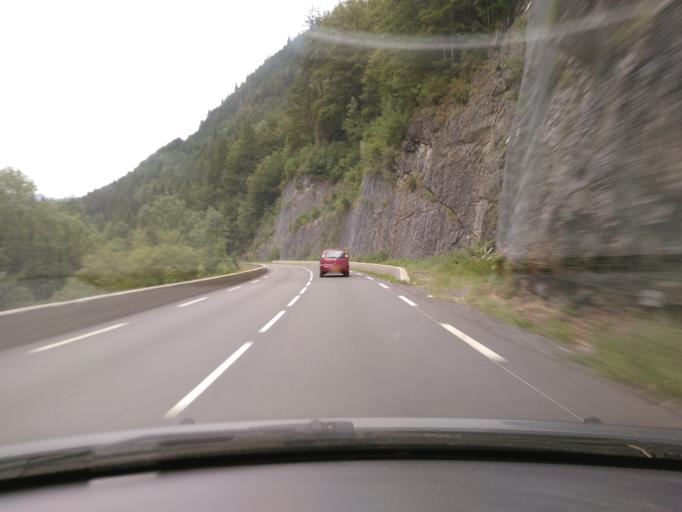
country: FR
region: Rhone-Alpes
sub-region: Departement de la Haute-Savoie
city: Saint-Jean-de-Sixt
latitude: 45.9425
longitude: 6.4031
